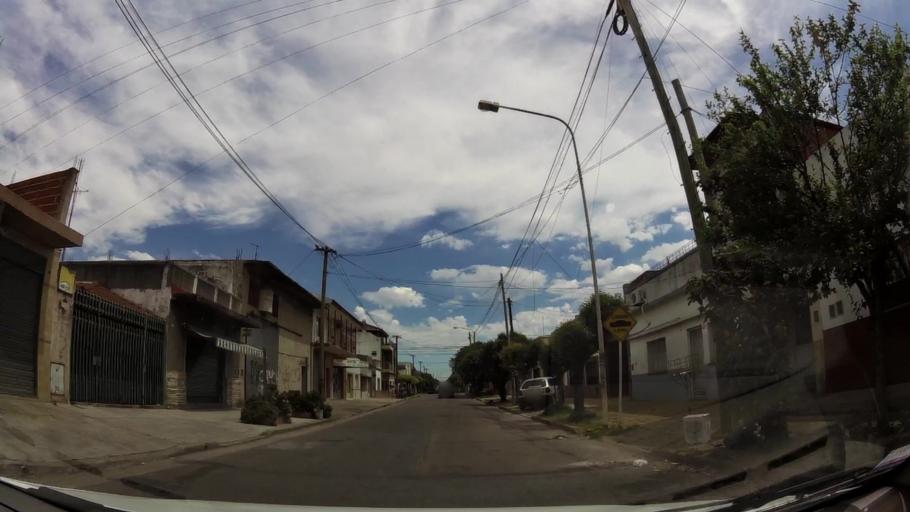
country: AR
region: Buenos Aires
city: San Justo
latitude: -34.6836
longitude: -58.5441
